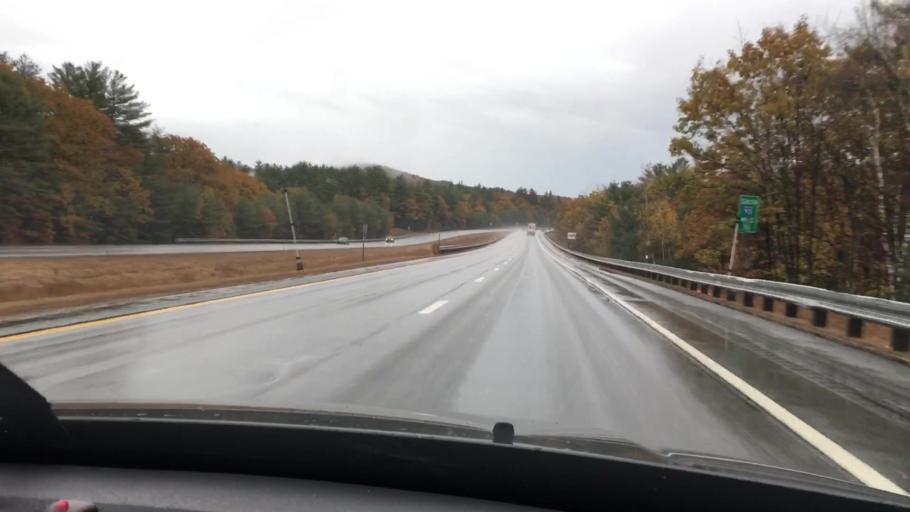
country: US
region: New Hampshire
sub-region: Grafton County
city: Ashland
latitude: 43.6238
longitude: -71.6489
